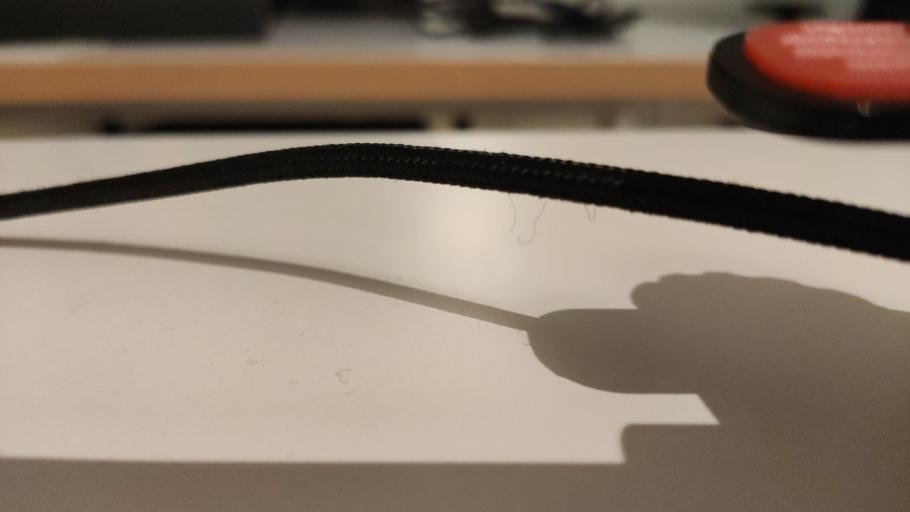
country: RU
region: Moskovskaya
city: Novosin'kovo
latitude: 56.3718
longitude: 37.3676
